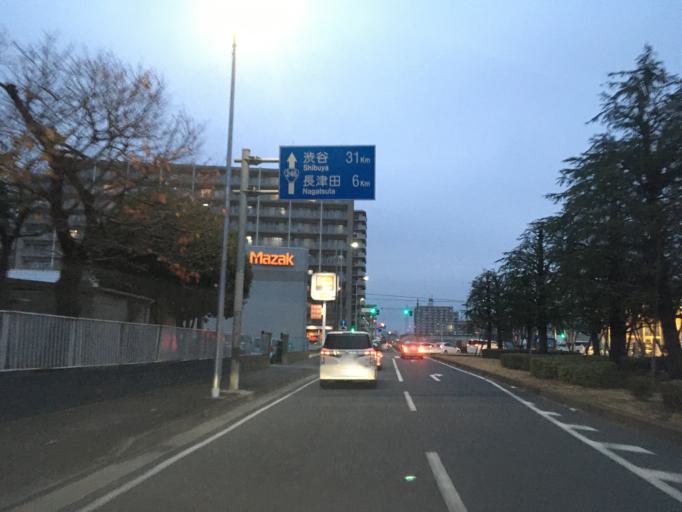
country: JP
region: Kanagawa
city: Minami-rinkan
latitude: 35.4881
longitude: 139.4637
